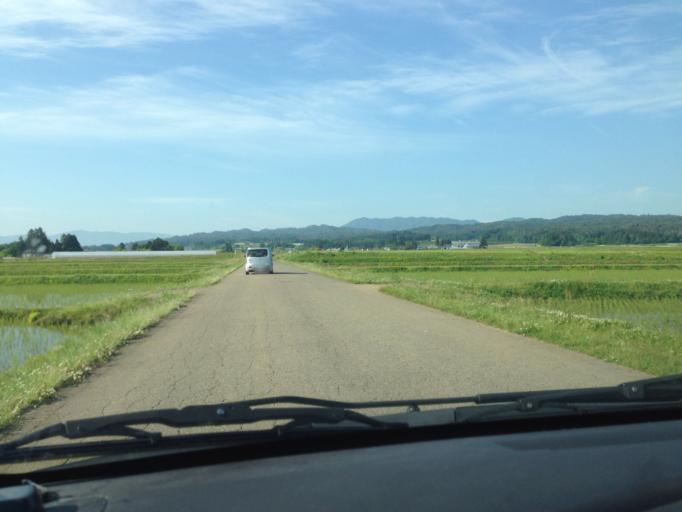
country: JP
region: Fukushima
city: Kitakata
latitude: 37.5371
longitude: 139.8104
